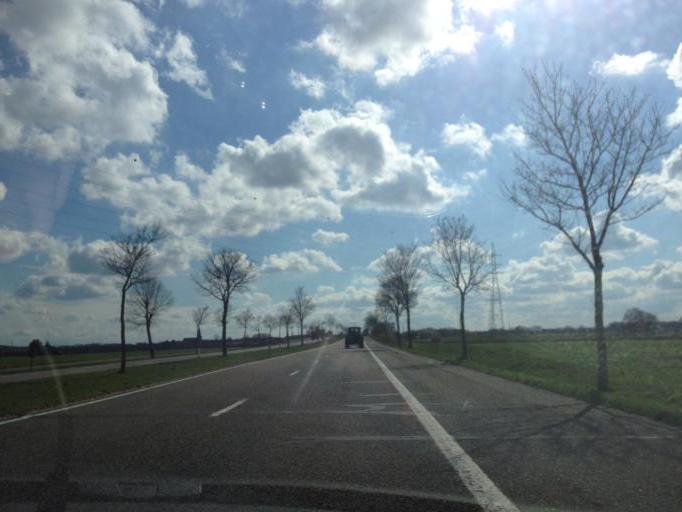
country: BE
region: Flanders
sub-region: Provincie Limburg
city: Bree
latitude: 51.1577
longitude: 5.5902
